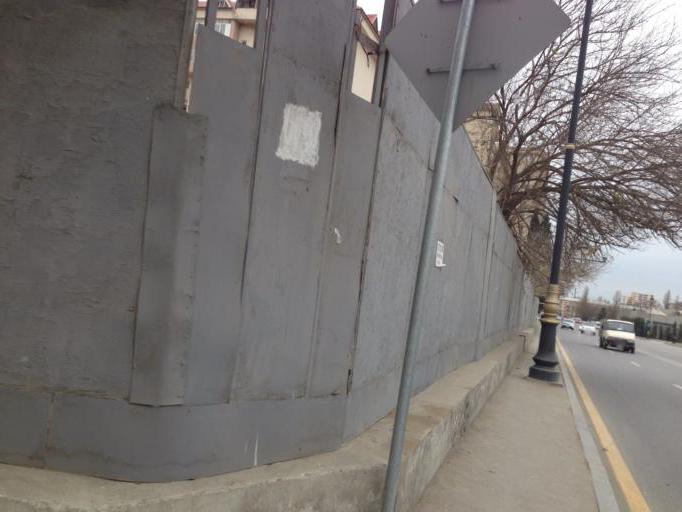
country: AZ
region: Baki
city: Baku
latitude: 40.3993
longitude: 49.8668
